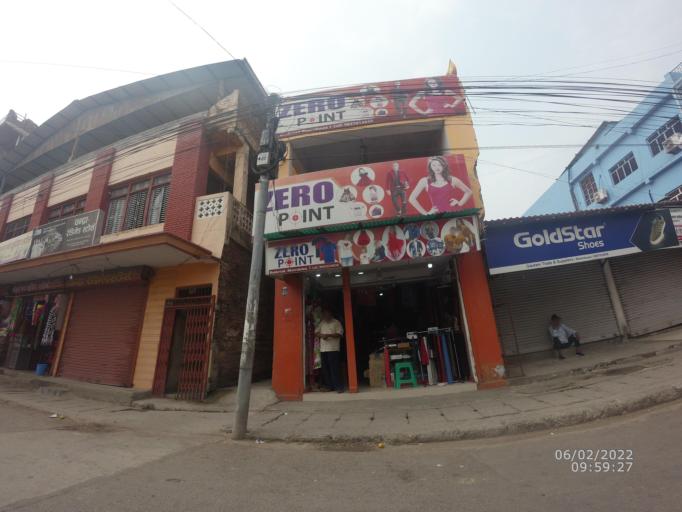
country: NP
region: Western Region
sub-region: Lumbini Zone
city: Bhairahawa
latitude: 27.5063
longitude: 83.4525
